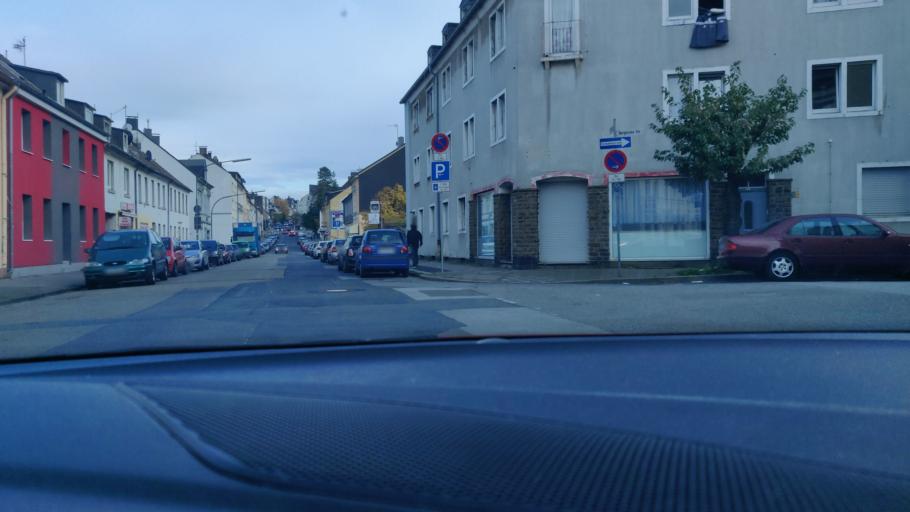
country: DE
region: North Rhine-Westphalia
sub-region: Regierungsbezirk Dusseldorf
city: Velbert
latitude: 51.3433
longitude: 7.0363
